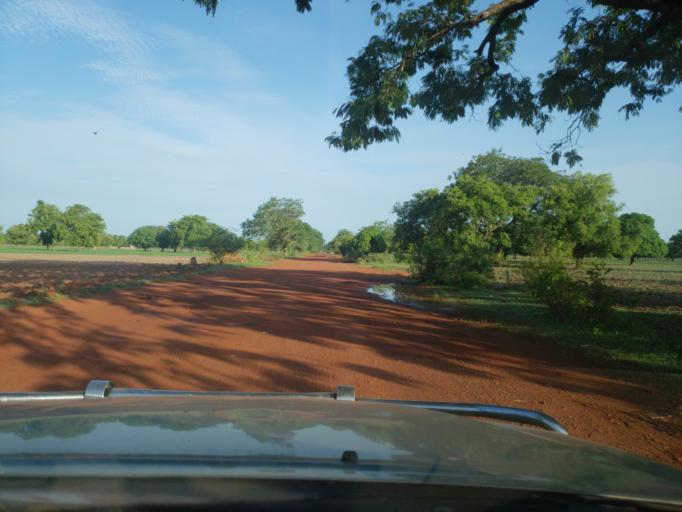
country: ML
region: Sikasso
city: Koutiala
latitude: 12.4094
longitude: -5.5521
